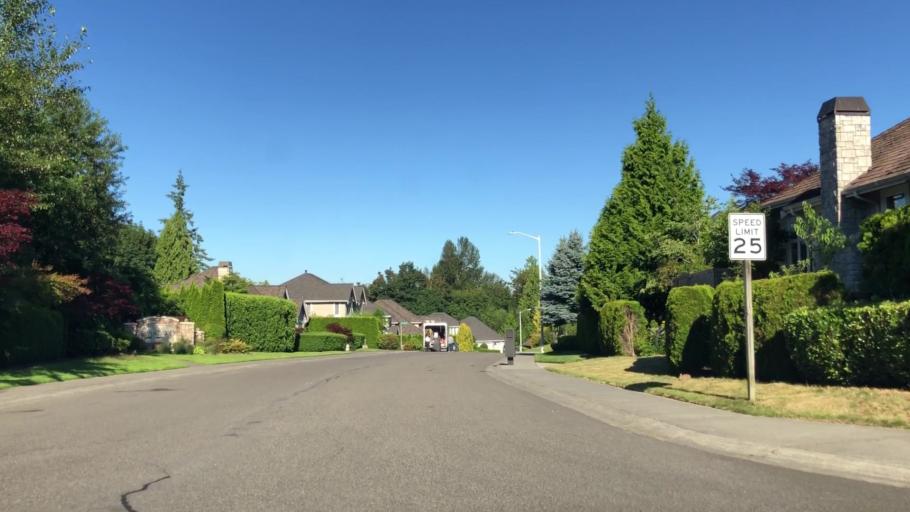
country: US
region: Washington
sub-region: Snohomish County
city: North Creek
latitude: 47.8141
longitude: -122.1969
